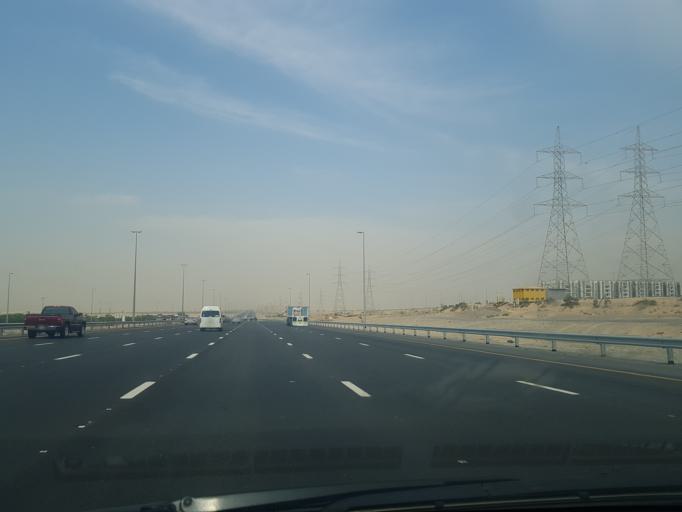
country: AE
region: Ash Shariqah
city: Sharjah
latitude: 25.2585
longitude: 55.5758
